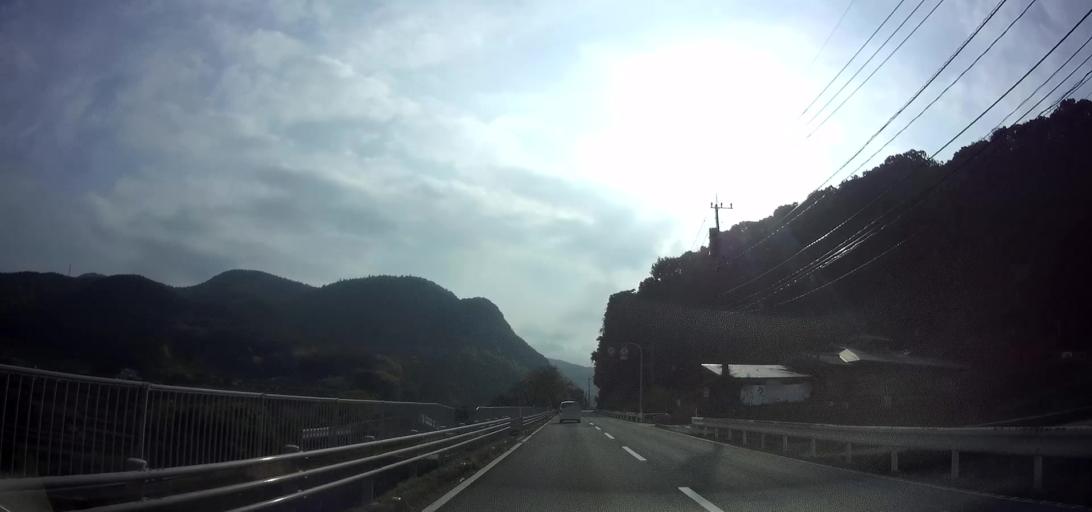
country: JP
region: Nagasaki
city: Shimabara
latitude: 32.7800
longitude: 130.2082
